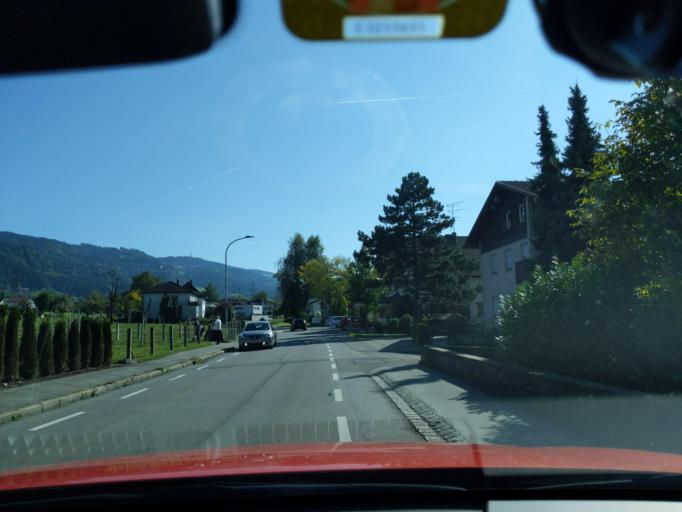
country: AT
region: Vorarlberg
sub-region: Politischer Bezirk Bregenz
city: Horbranz
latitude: 47.5537
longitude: 9.7506
